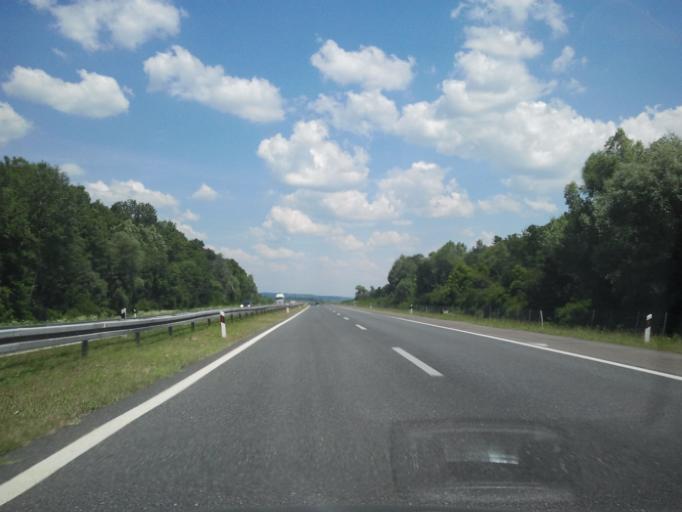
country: HR
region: Brodsko-Posavska
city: Oriovac
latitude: 45.1593
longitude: 17.8360
